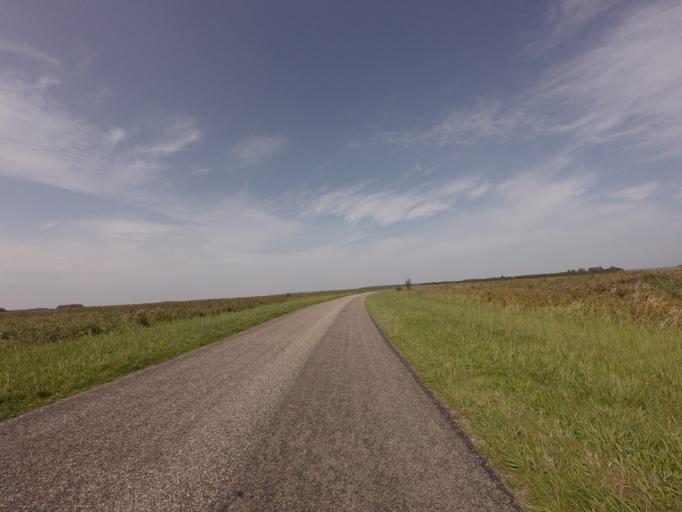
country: NL
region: Groningen
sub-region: Gemeente De Marne
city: Ulrum
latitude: 53.3484
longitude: 6.2675
